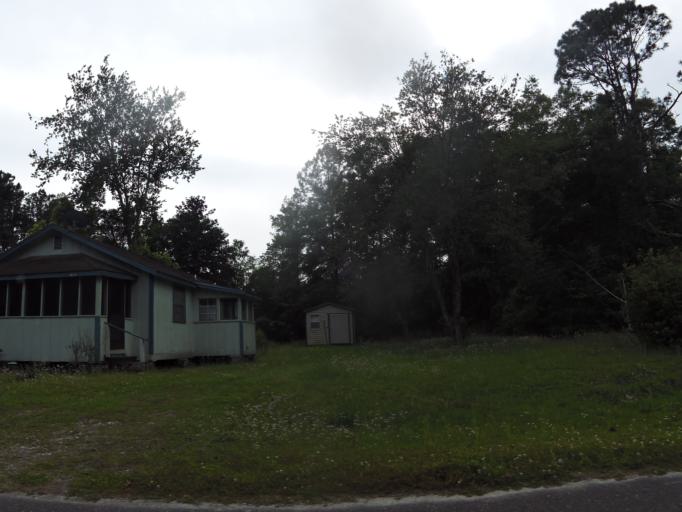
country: US
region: Florida
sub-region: Nassau County
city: Hilliard
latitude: 30.6946
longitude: -81.9252
